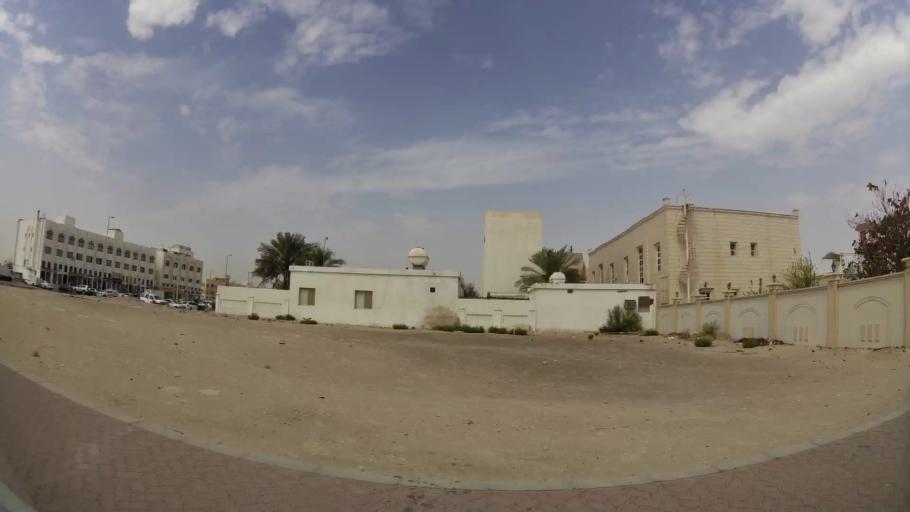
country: AE
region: Abu Dhabi
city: Abu Dhabi
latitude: 24.3057
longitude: 54.6145
